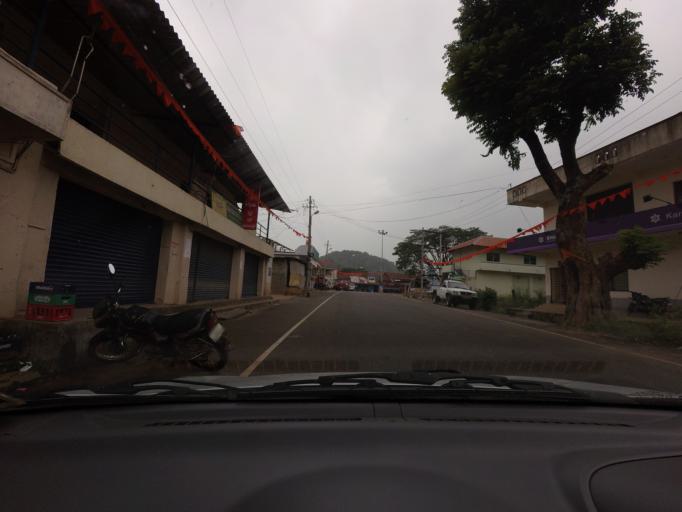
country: IN
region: Karnataka
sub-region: Hassan
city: Sakleshpur
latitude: 13.0042
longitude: 75.6976
